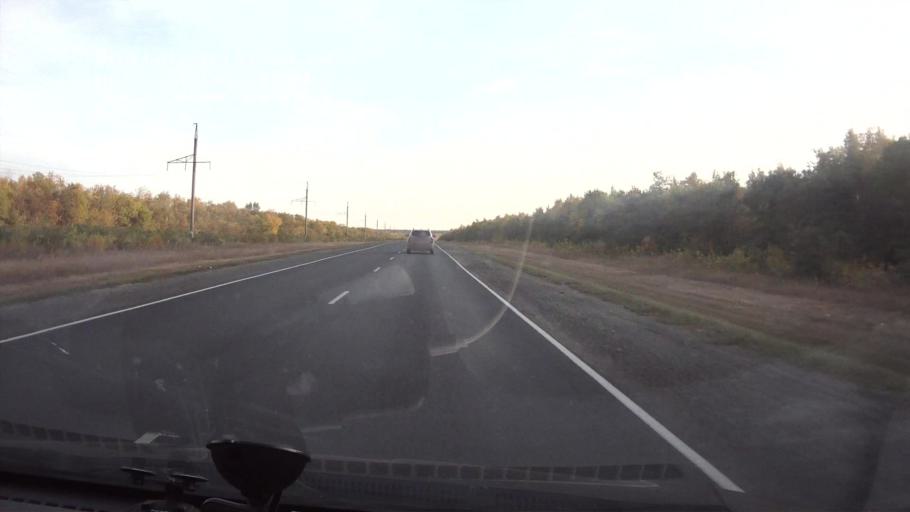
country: RU
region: Saratov
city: Krasnoarmeysk
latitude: 51.1188
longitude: 45.6507
